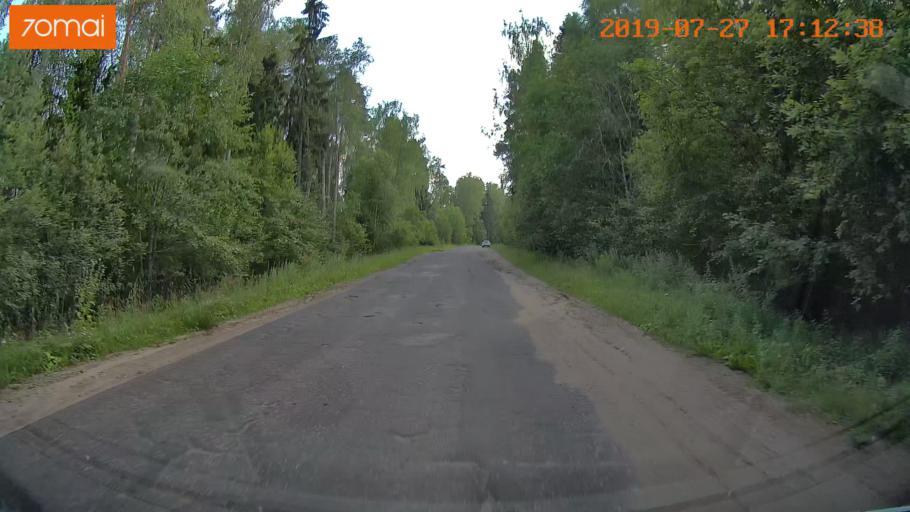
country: RU
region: Ivanovo
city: Novo-Talitsy
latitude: 57.0567
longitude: 40.8600
